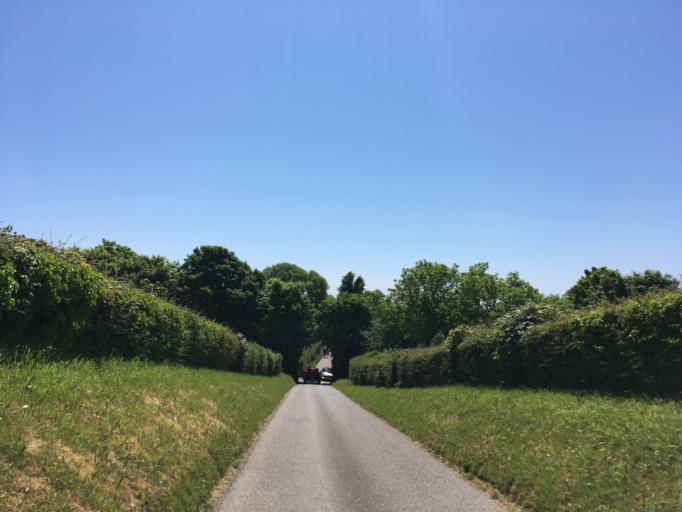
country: GB
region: England
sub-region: Devon
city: Dartmouth
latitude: 50.3501
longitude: -3.5373
